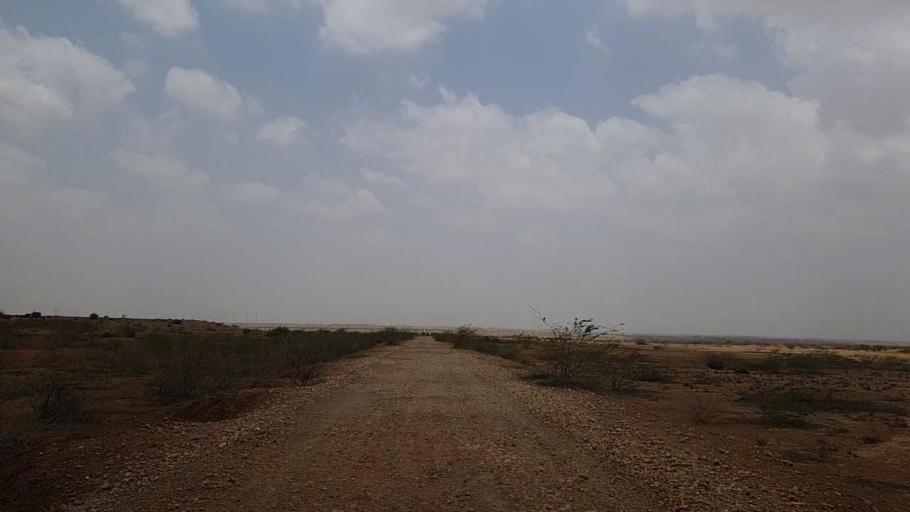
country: PK
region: Sindh
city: Thatta
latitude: 24.8993
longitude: 67.8982
